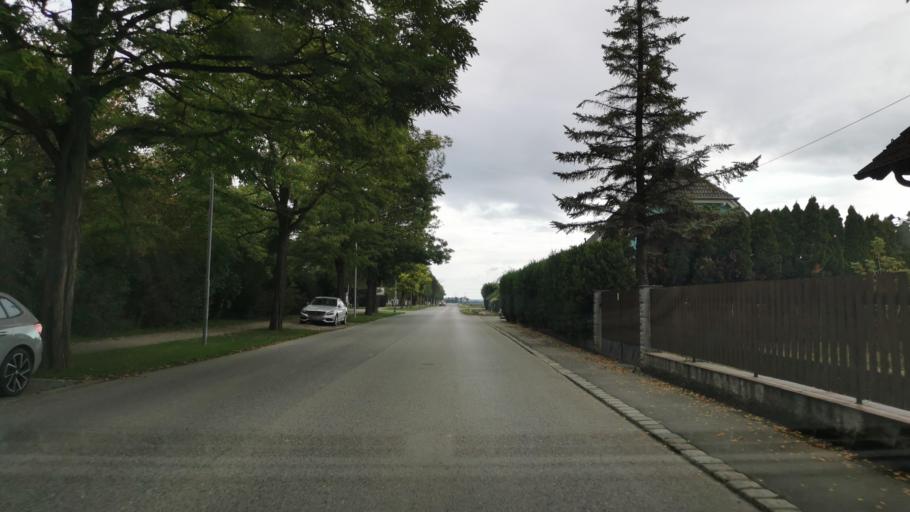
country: AT
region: Lower Austria
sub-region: Politischer Bezirk Ganserndorf
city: Raasdorf
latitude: 48.2494
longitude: 16.5617
